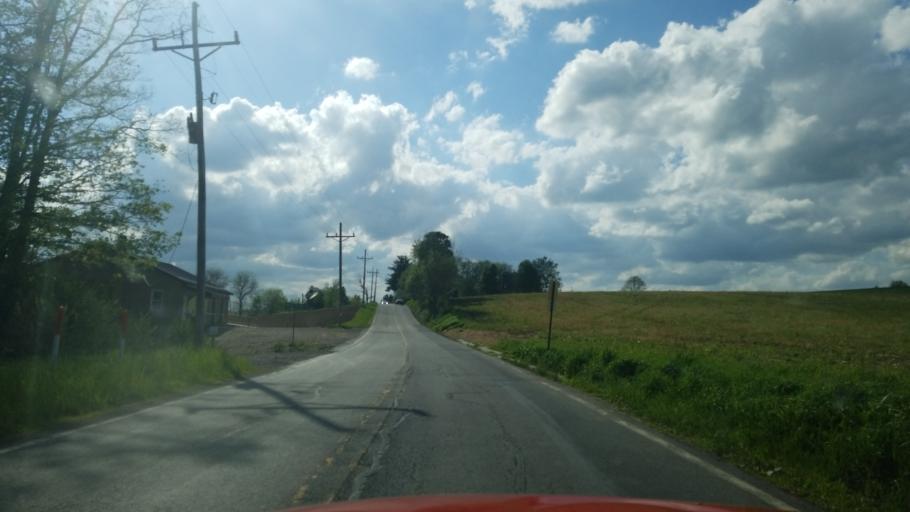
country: US
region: Pennsylvania
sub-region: Clearfield County
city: Hyde
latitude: 40.9770
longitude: -78.4666
